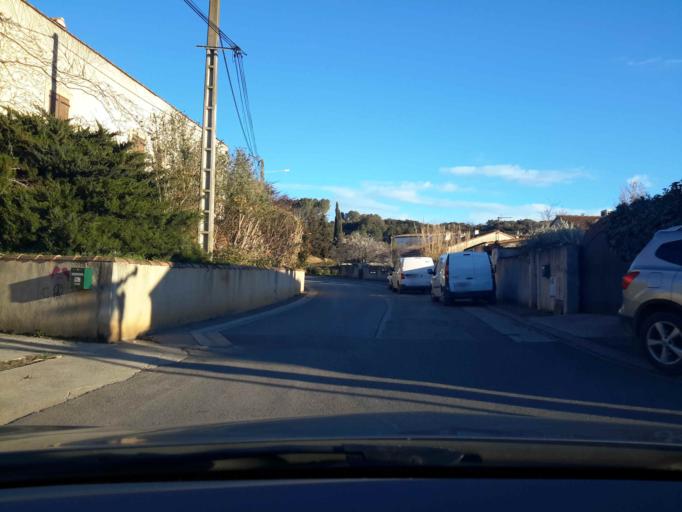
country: FR
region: Languedoc-Roussillon
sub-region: Departement du Gard
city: Beauvoisin
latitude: 43.7159
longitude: 4.3271
